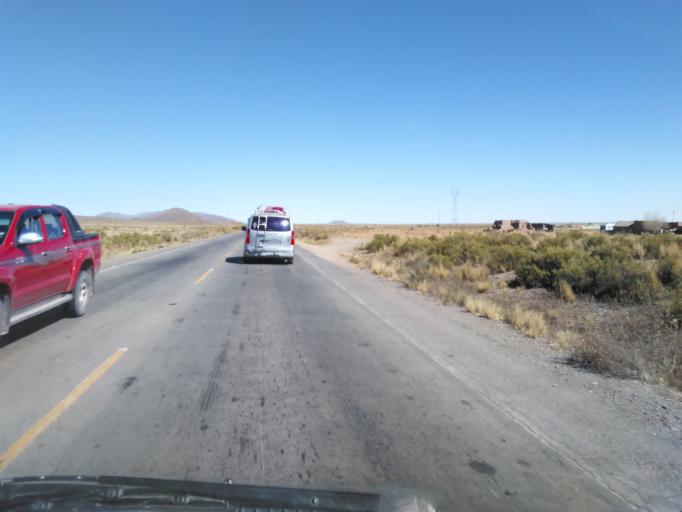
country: BO
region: Oruro
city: Machacamarca
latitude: -18.0691
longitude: -67.0057
